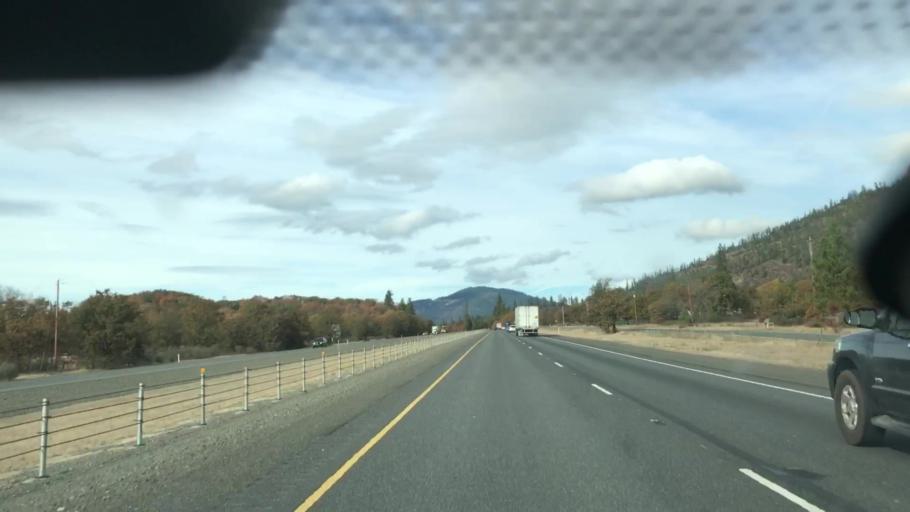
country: US
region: Oregon
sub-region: Josephine County
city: Merlin
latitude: 42.5079
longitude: -123.3631
